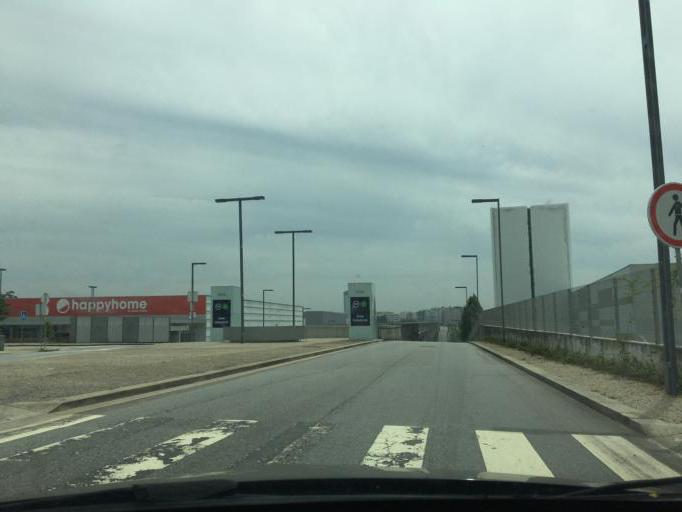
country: PT
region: Porto
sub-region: Maia
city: Maia
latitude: 41.2446
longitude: -8.6290
